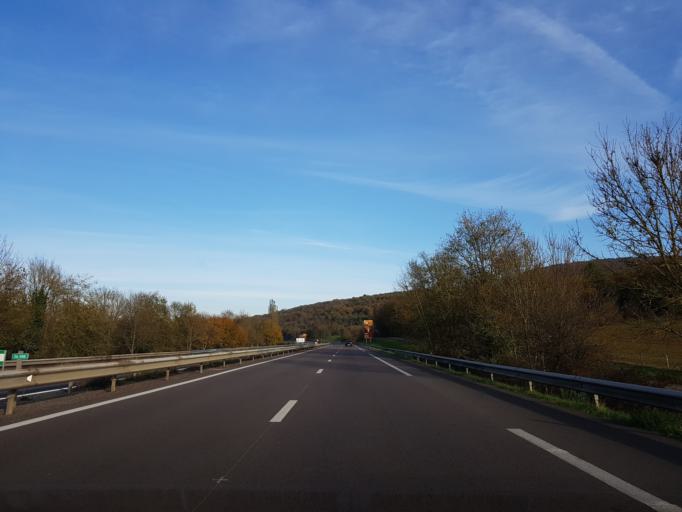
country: FR
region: Bourgogne
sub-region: Departement de la Cote-d'Or
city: Fleurey-sur-Ouche
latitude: 47.3085
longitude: 4.8728
